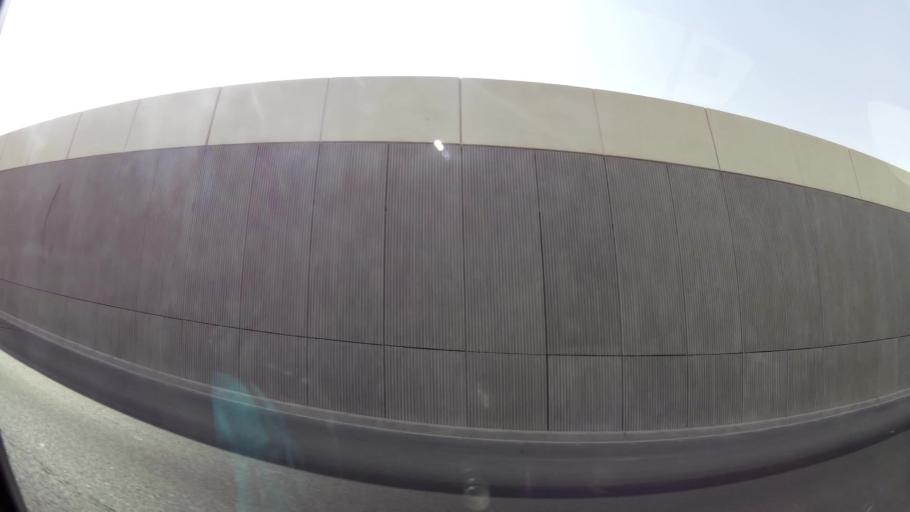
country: KW
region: Muhafazat al Jahra'
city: Al Jahra'
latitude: 29.3114
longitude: 47.6557
